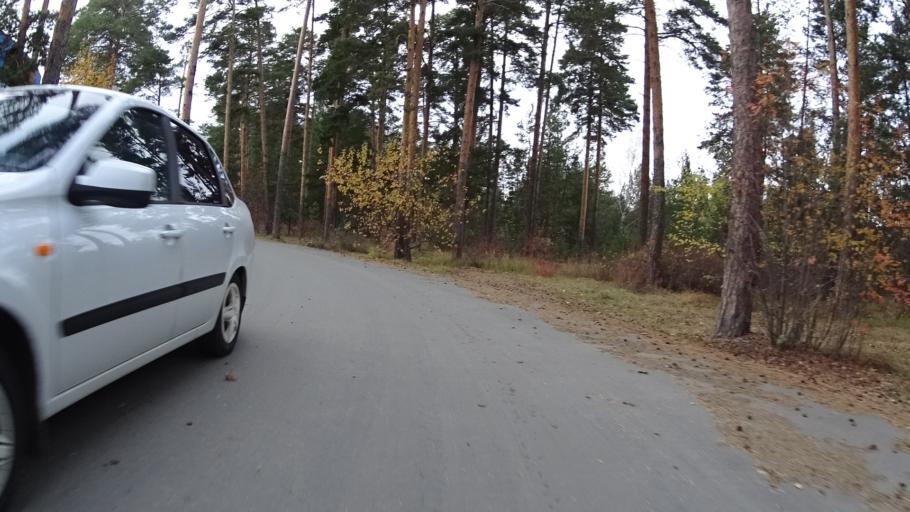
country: RU
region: Chelyabinsk
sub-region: Gorod Chelyabinsk
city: Chelyabinsk
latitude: 55.1683
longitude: 61.3637
